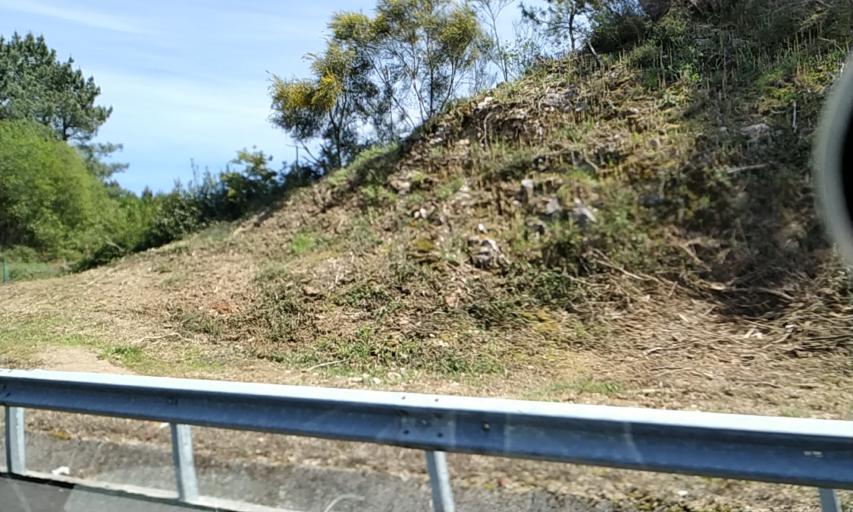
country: ES
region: Galicia
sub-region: Provincia de Pontevedra
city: Caldas de Reis
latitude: 42.6367
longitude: -8.6574
